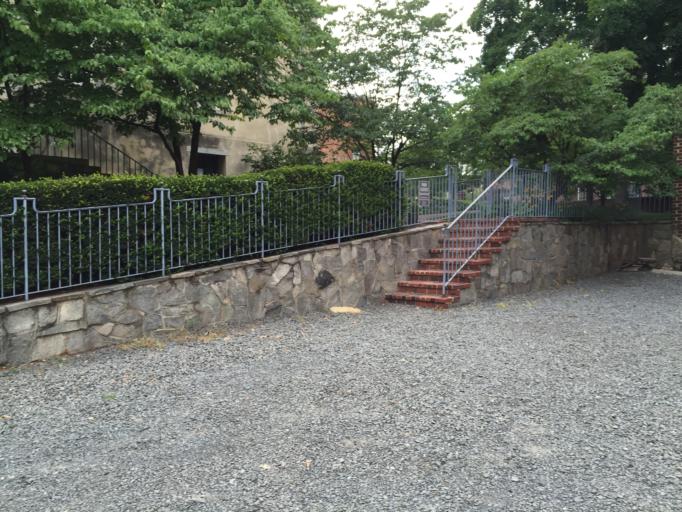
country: US
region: Virginia
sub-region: City of Alexandria
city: Alexandria
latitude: 38.8054
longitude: -77.0417
